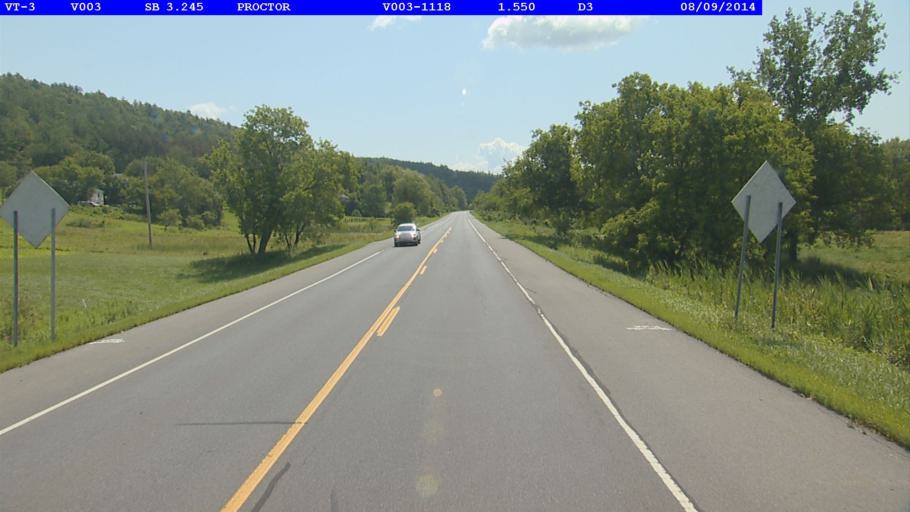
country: US
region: Vermont
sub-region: Rutland County
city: West Rutland
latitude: 43.6461
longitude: -73.0336
